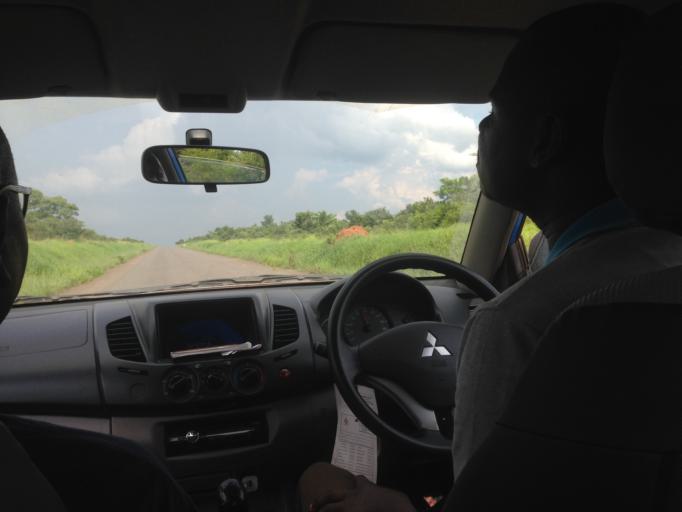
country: UG
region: Northern Region
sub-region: Nwoya District
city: Nwoya
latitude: 2.4114
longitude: 32.0094
